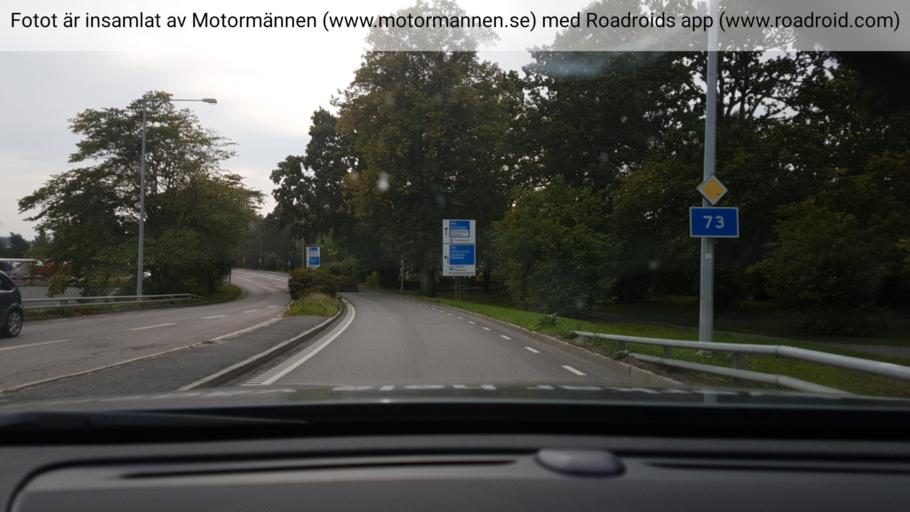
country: SE
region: Stockholm
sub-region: Nynashamns Kommun
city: Nynashamn
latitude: 58.9085
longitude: 17.9545
